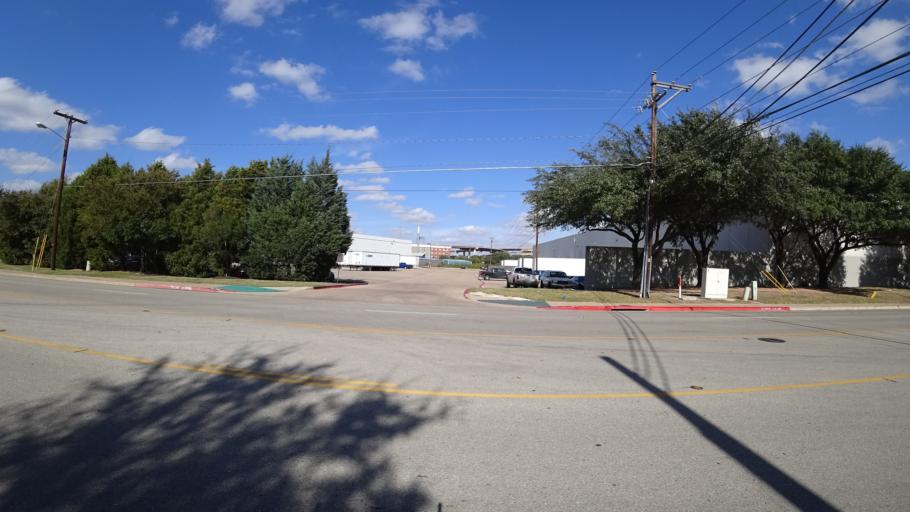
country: US
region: Texas
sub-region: Travis County
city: Wells Branch
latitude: 30.4763
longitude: -97.6783
